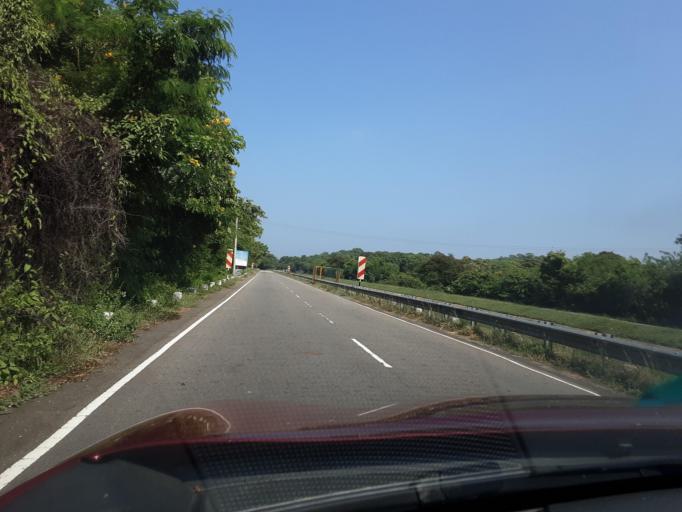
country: LK
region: Uva
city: Badulla
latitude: 7.2786
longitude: 81.0444
